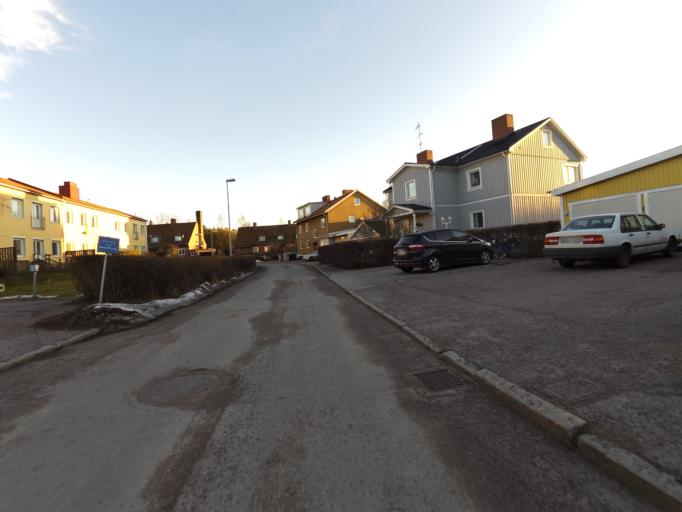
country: SE
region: Gaevleborg
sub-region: Gavle Kommun
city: Gavle
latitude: 60.6666
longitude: 17.1238
